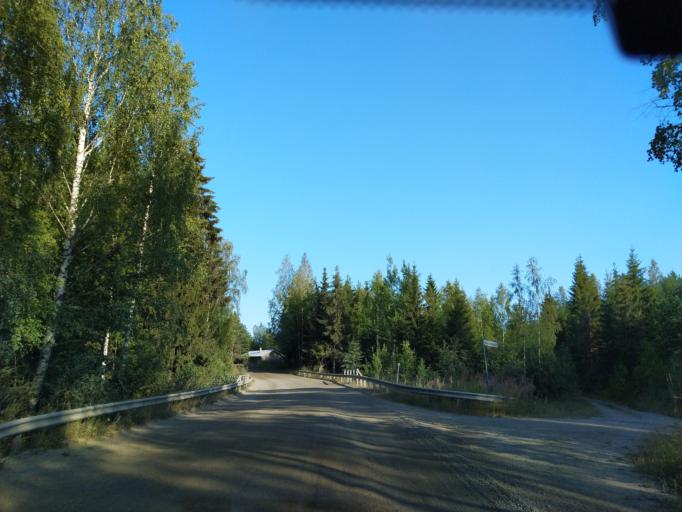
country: FI
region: Central Finland
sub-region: Jaemsae
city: Kuhmoinen
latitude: 61.6049
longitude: 25.1352
